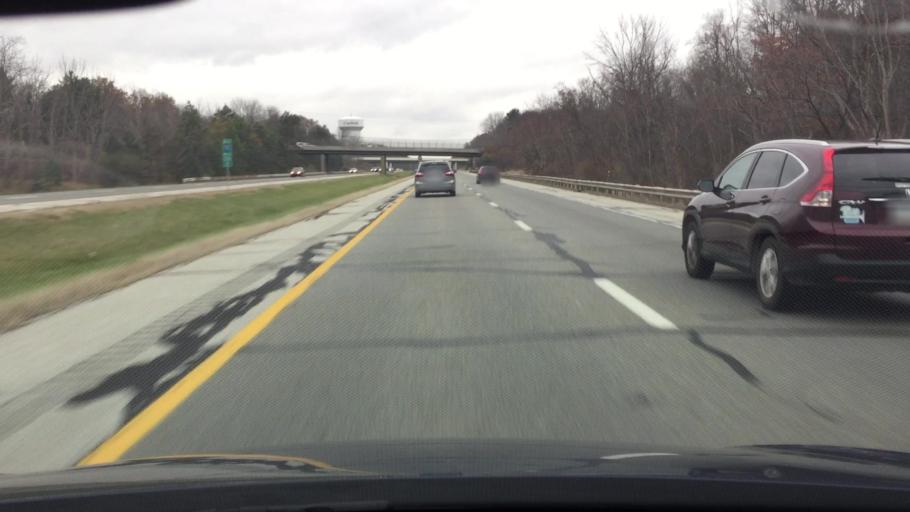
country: US
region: Ohio
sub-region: Mahoning County
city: Canfield
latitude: 41.0308
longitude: -80.7343
